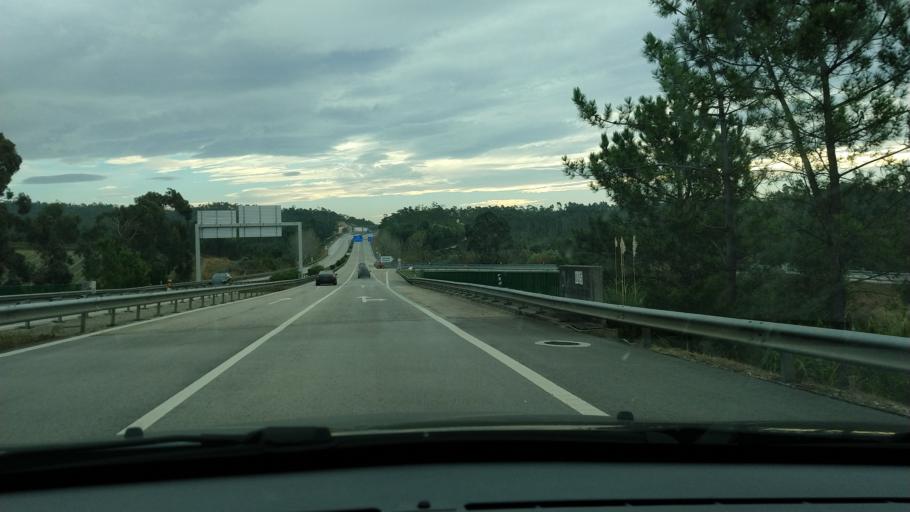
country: PT
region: Coimbra
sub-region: Figueira da Foz
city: Alhadas
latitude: 40.1537
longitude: -8.7956
